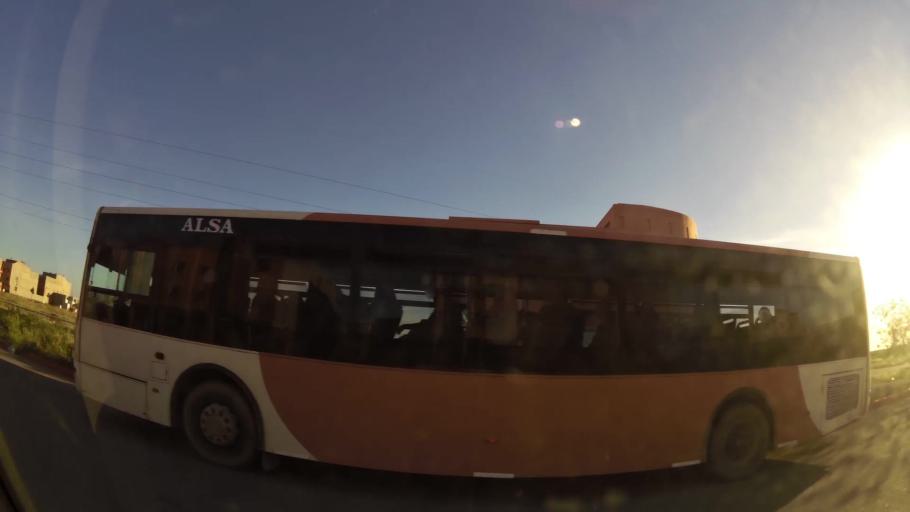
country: MA
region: Marrakech-Tensift-Al Haouz
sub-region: Marrakech
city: Marrakesh
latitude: 31.7435
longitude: -8.1242
